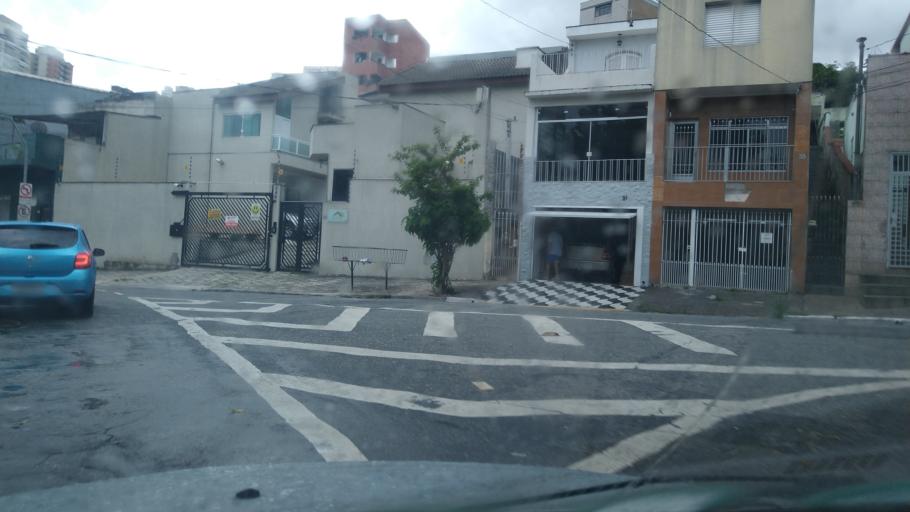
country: BR
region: Sao Paulo
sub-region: Sao Paulo
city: Sao Paulo
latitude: -23.5621
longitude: -46.5759
